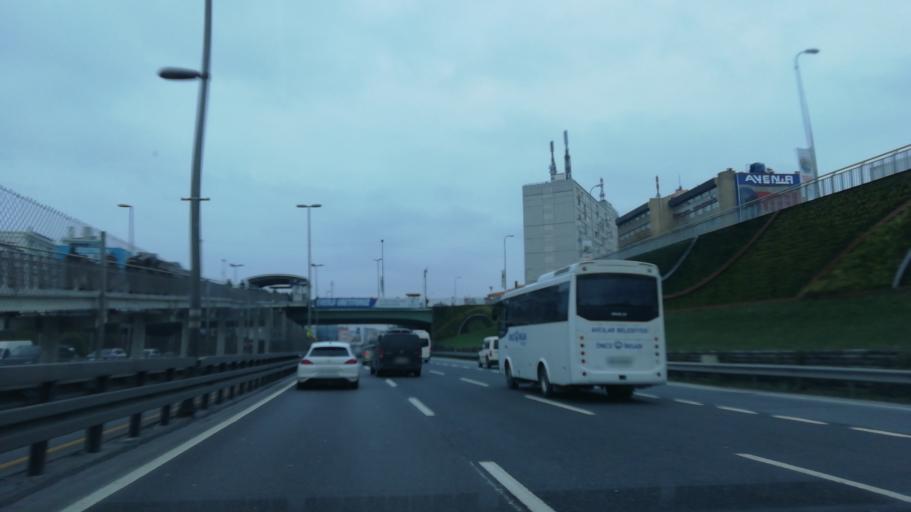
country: TR
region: Istanbul
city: Sisli
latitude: 41.0625
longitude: 28.9680
